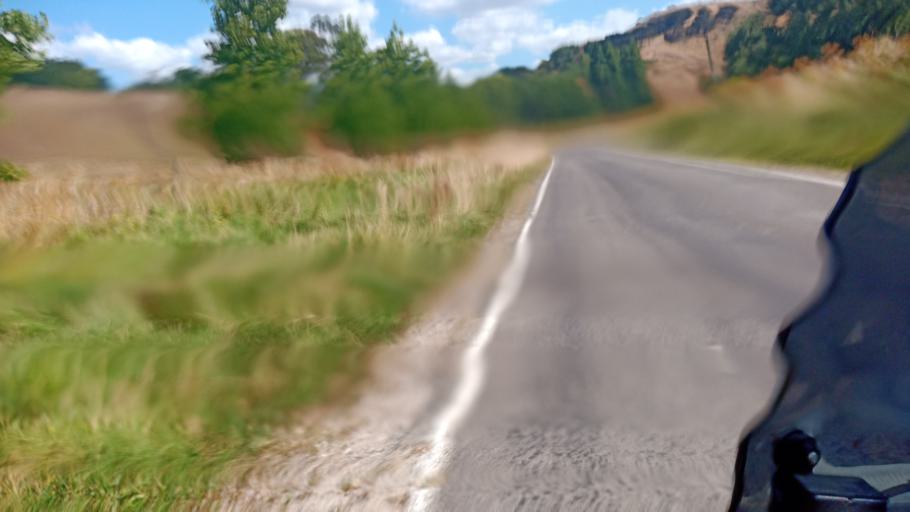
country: NZ
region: Gisborne
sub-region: Gisborne District
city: Gisborne
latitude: -38.5978
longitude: 177.7765
